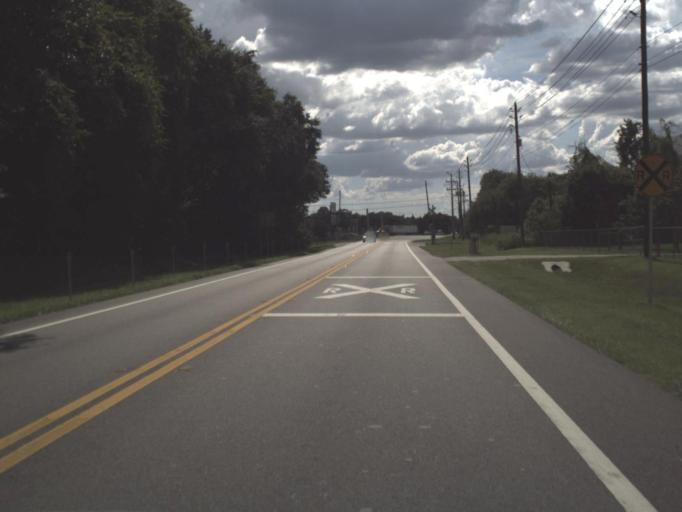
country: US
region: Florida
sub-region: Polk County
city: Winston
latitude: 28.0281
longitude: -82.0522
